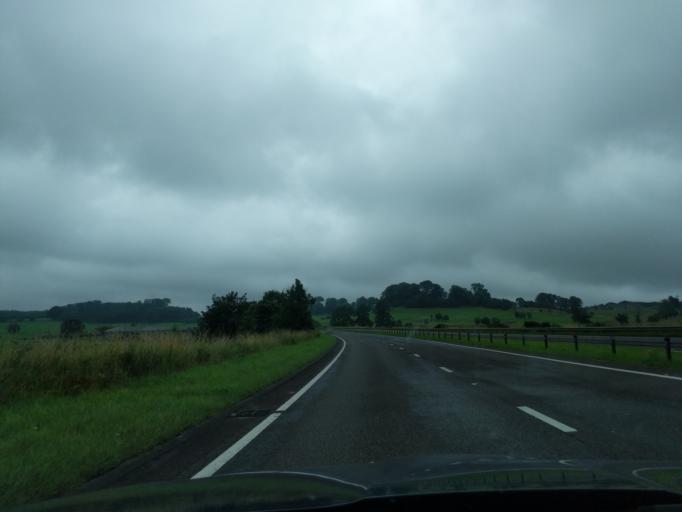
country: GB
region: England
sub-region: Northumberland
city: Alnwick
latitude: 55.4148
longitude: -1.6767
